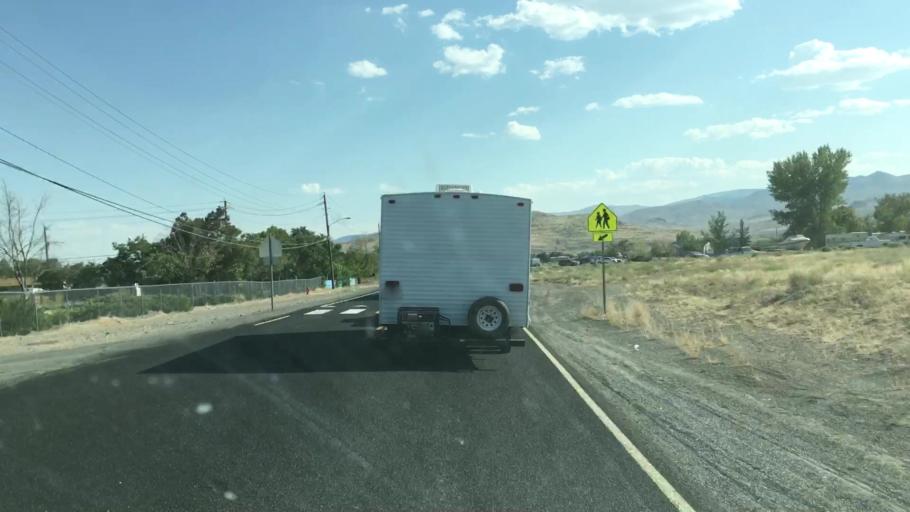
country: US
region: Nevada
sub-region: Lyon County
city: Fernley
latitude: 39.6356
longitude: -119.2906
